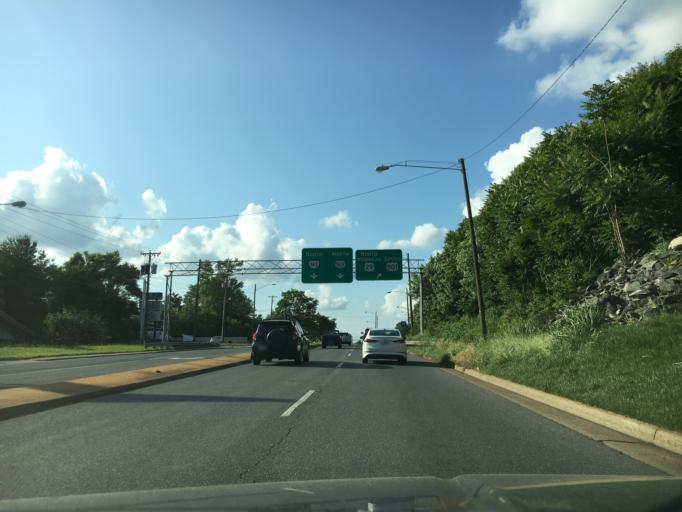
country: US
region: Virginia
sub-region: City of Lynchburg
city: West Lynchburg
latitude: 37.3627
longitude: -79.1815
